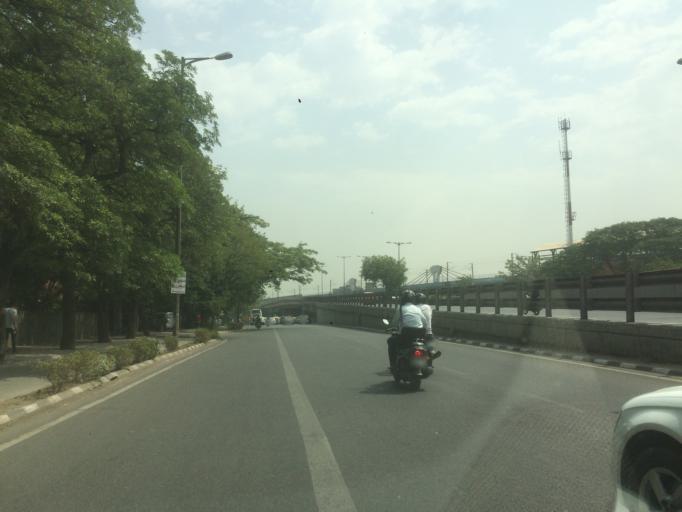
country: IN
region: NCT
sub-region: New Delhi
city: New Delhi
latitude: 28.5637
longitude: 77.2329
